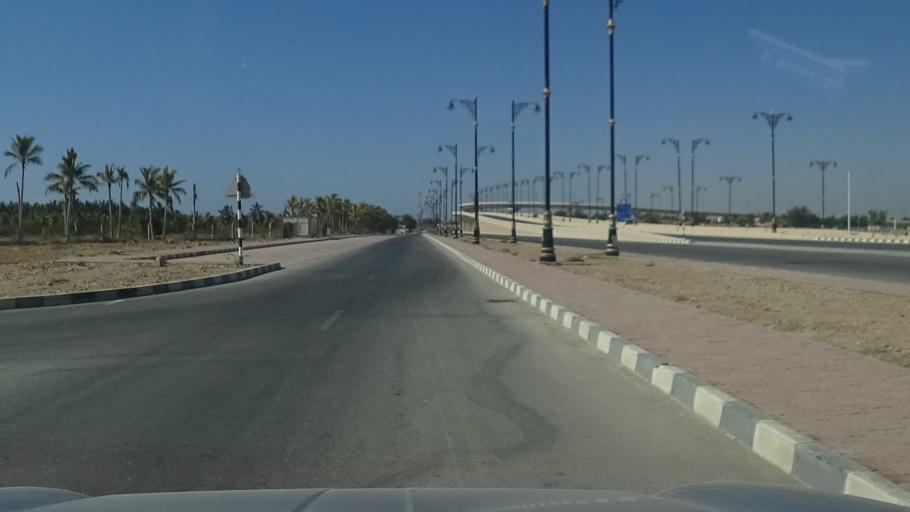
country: OM
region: Zufar
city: Salalah
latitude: 17.0352
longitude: 54.1473
